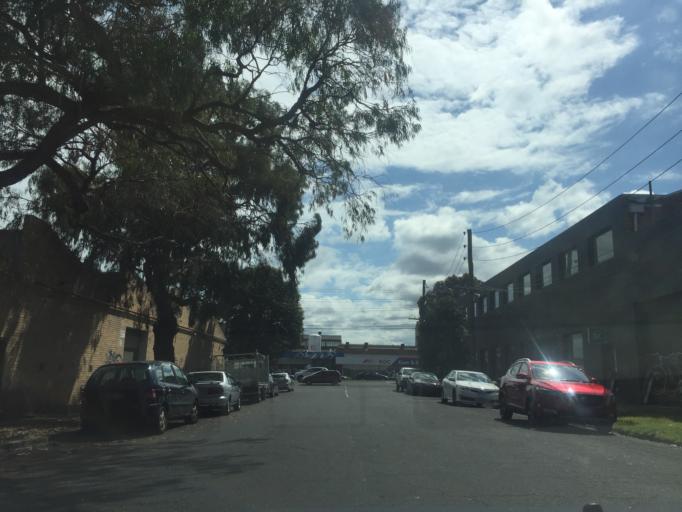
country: AU
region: Victoria
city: Heidelberg West
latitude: -37.7487
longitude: 145.0280
